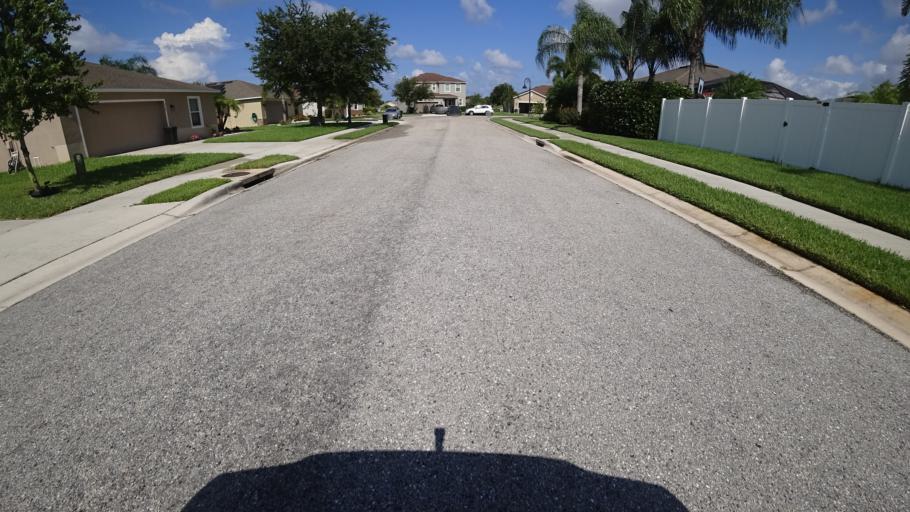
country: US
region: Florida
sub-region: Manatee County
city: Whitfield
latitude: 27.4267
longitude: -82.5597
